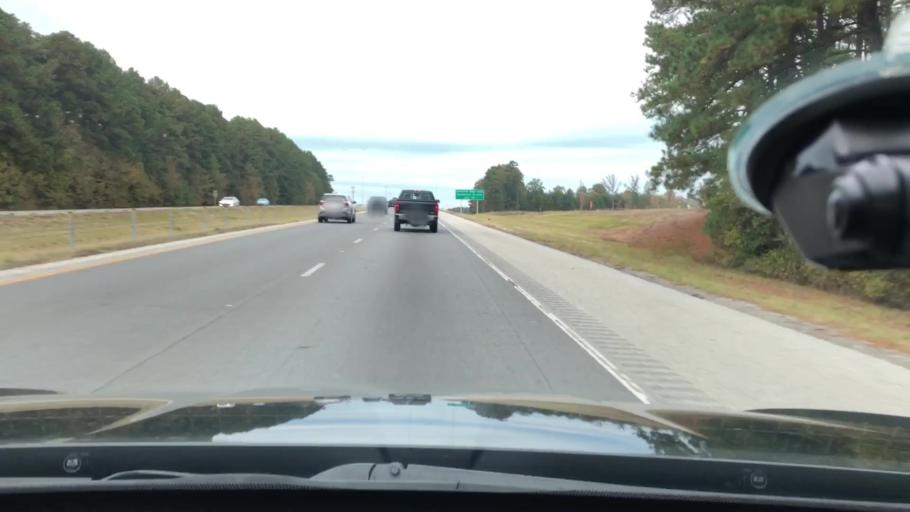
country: US
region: Arkansas
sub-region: Clark County
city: Arkadelphia
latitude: 34.1093
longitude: -93.0977
